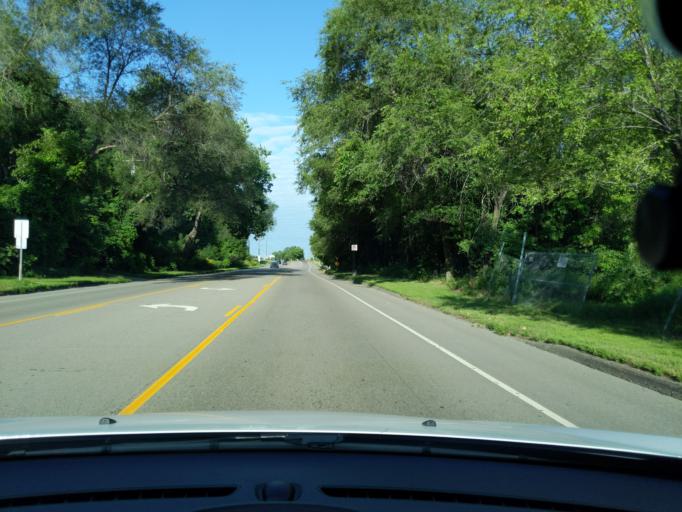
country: US
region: Minnesota
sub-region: Ramsey County
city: Falcon Heights
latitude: 44.9688
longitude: -93.1787
